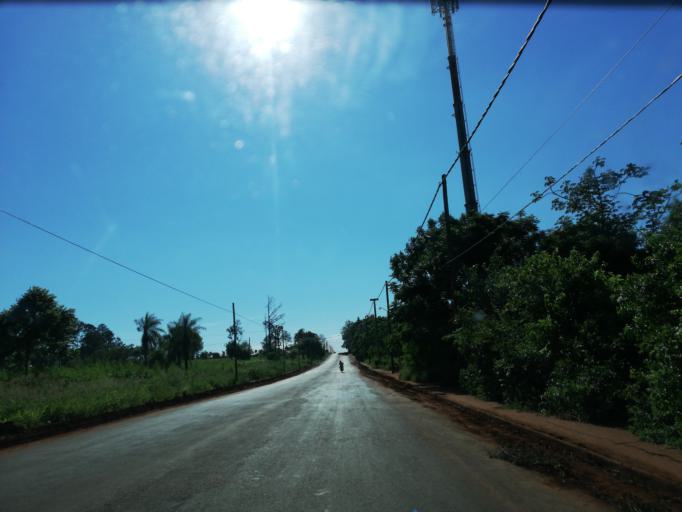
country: AR
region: Misiones
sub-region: Departamento de Capital
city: Posadas
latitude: -27.4338
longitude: -55.9341
